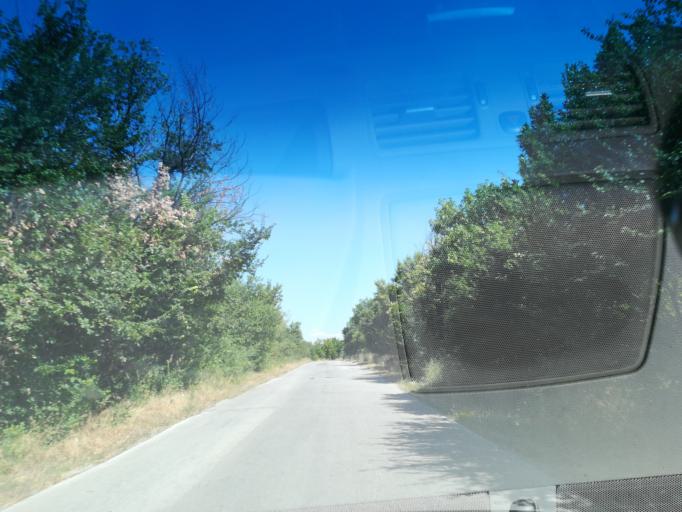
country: BG
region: Plovdiv
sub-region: Obshtina Sadovo
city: Sadovo
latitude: 42.0158
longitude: 25.0369
